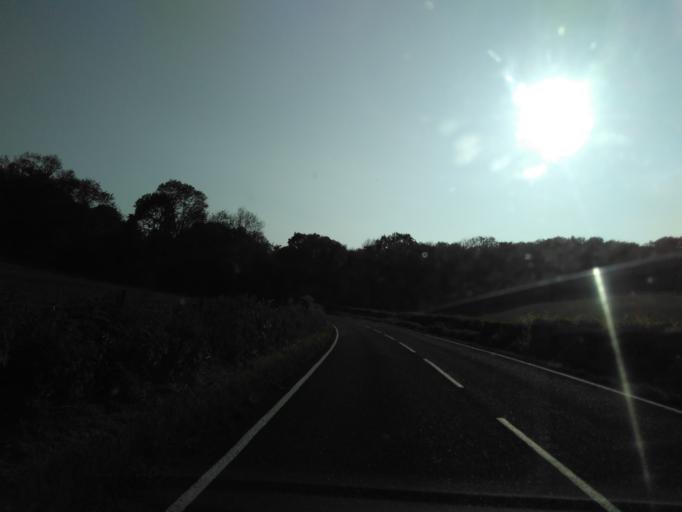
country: GB
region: England
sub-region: Kent
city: Wye
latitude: 51.2375
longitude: 0.9347
